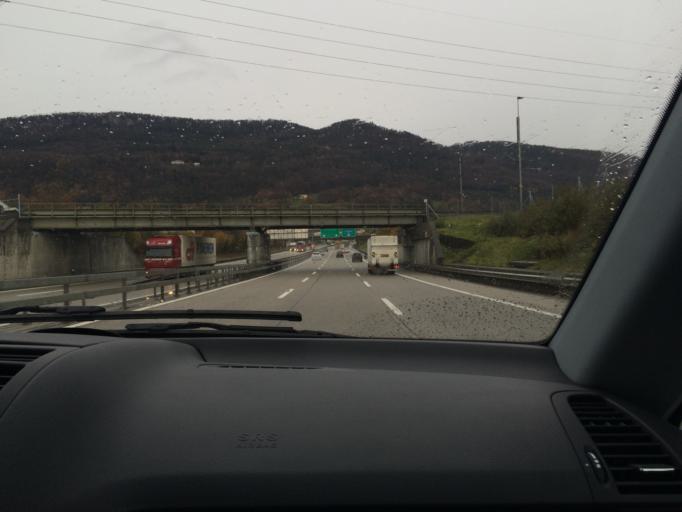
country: CH
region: Solothurn
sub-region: Bezirk Gaeu
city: Egerkingen
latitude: 47.3167
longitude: 7.8062
